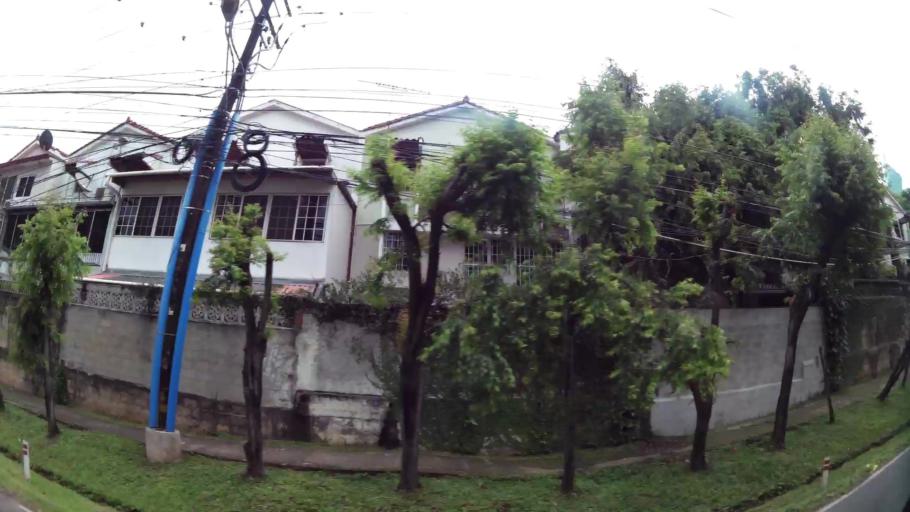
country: PA
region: Panama
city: Panama
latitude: 8.9872
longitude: -79.5152
